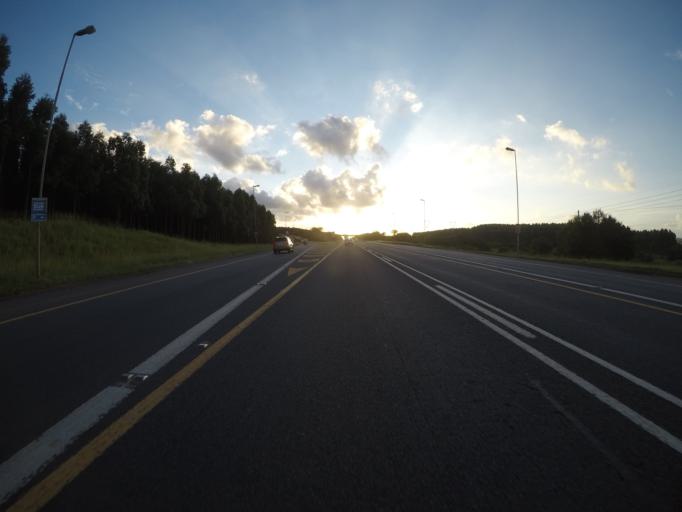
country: ZA
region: KwaZulu-Natal
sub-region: uThungulu District Municipality
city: Richards Bay
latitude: -28.6932
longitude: 32.0333
